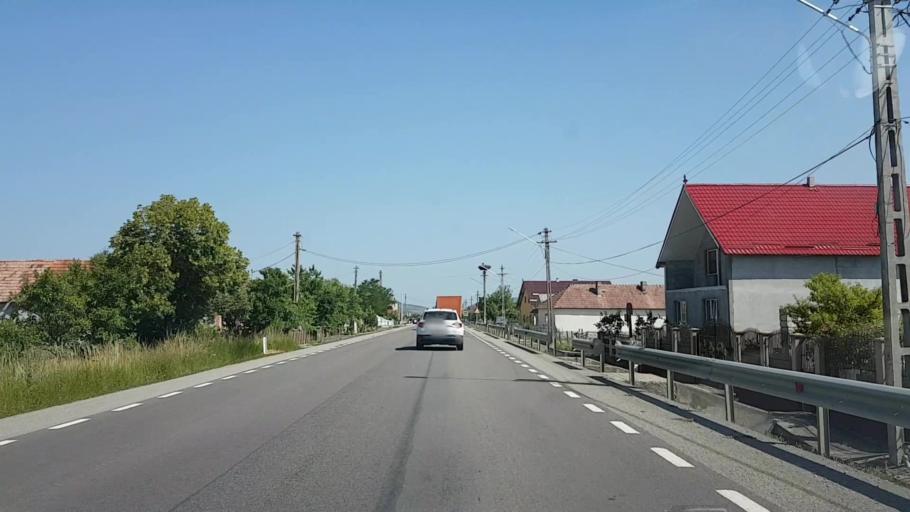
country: RO
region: Bistrita-Nasaud
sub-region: Comuna Sieu-Odorhei
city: Sieu-Odorhei
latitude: 47.1180
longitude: 24.3323
